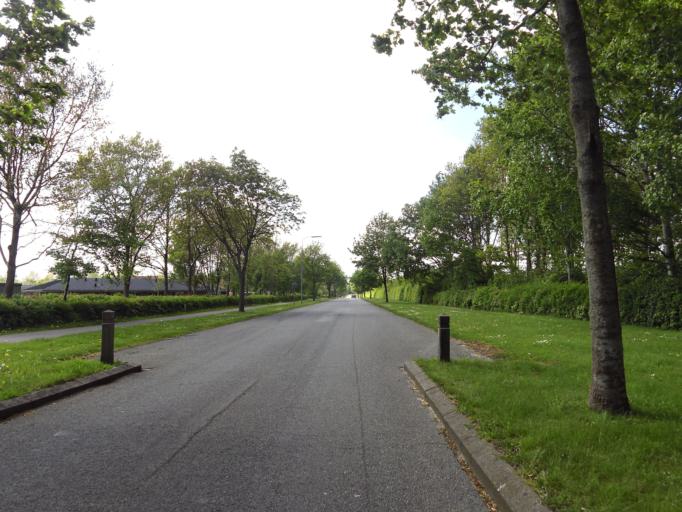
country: DK
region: South Denmark
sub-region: Tonder Kommune
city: Toftlund
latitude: 55.1831
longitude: 9.0818
